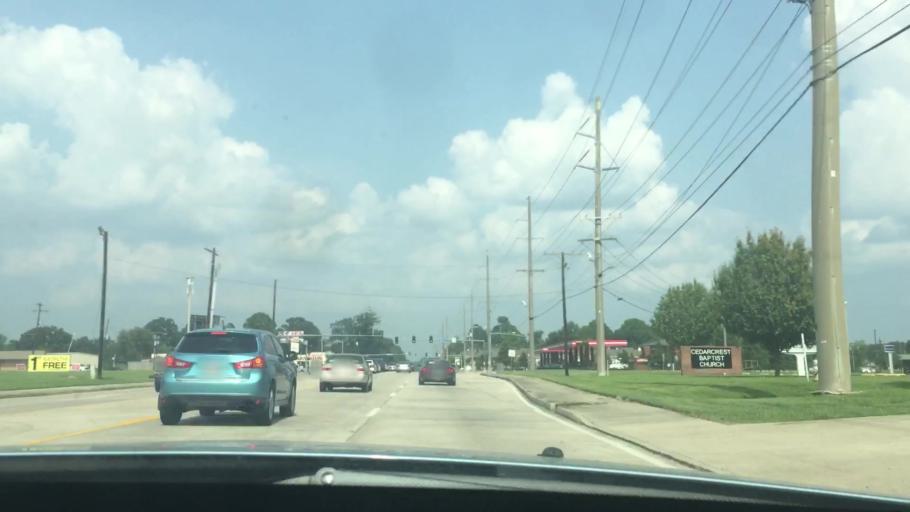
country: US
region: Louisiana
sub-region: East Baton Rouge Parish
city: Westminster
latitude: 30.4337
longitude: -91.0691
